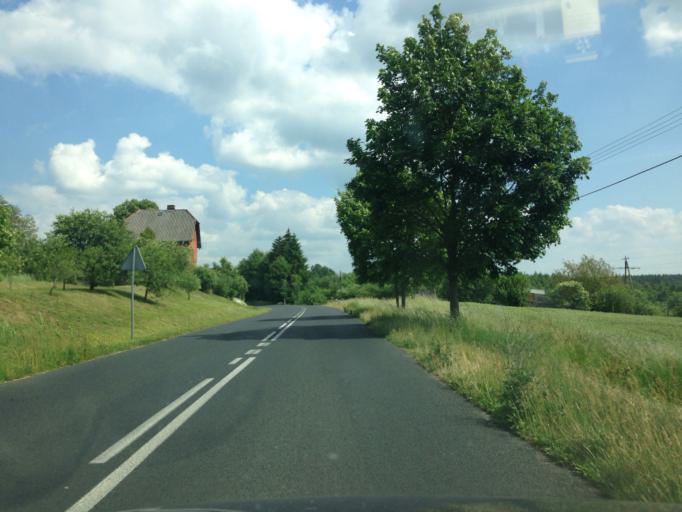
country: PL
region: Kujawsko-Pomorskie
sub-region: Powiat brodnicki
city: Bartniczka
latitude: 53.2480
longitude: 19.6155
